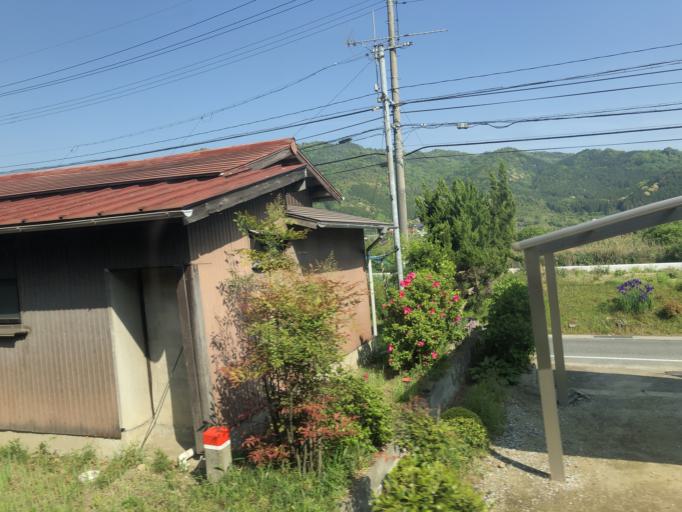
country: JP
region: Yamaguchi
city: Ogori-shimogo
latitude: 34.1202
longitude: 131.4042
